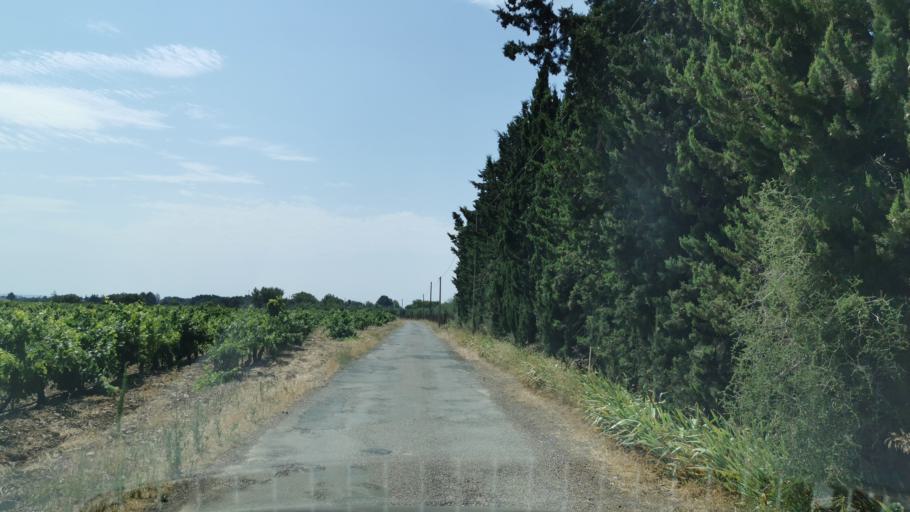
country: FR
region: Languedoc-Roussillon
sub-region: Departement de l'Aude
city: Bize-Minervois
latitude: 43.3001
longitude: 2.8752
